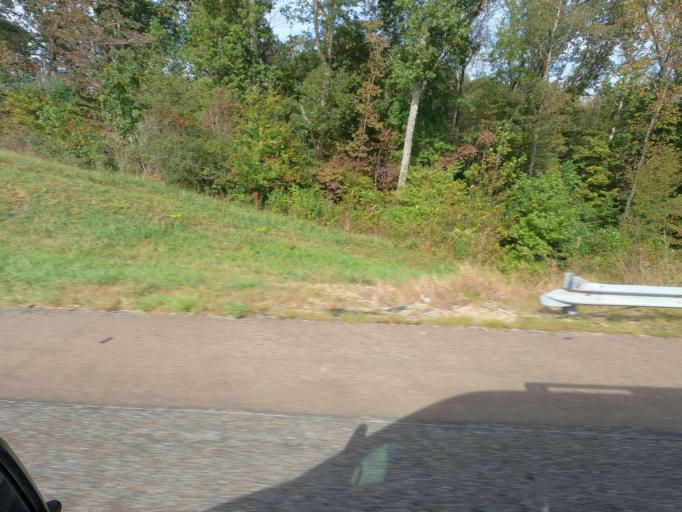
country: US
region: Tennessee
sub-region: Humphreys County
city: New Johnsonville
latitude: 35.8678
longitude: -88.0358
